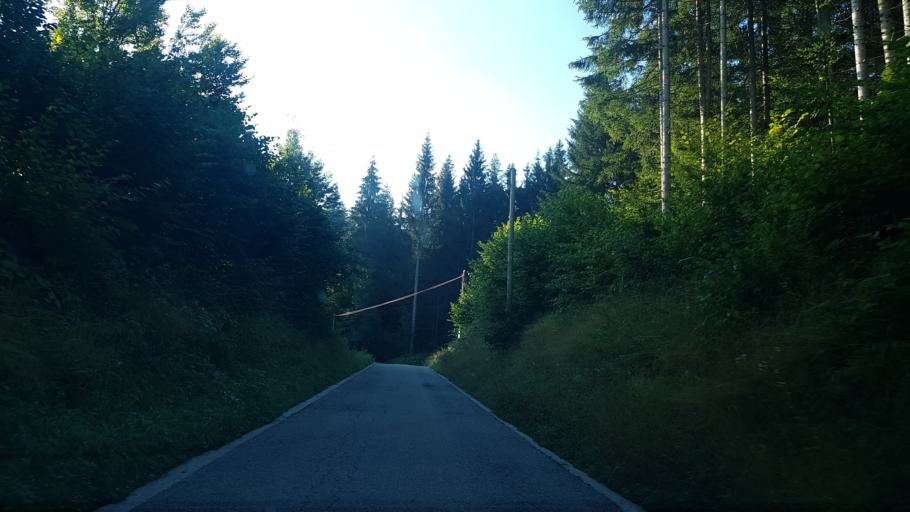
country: IT
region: Friuli Venezia Giulia
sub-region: Provincia di Udine
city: Tarvisio
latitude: 46.4905
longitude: 13.6027
